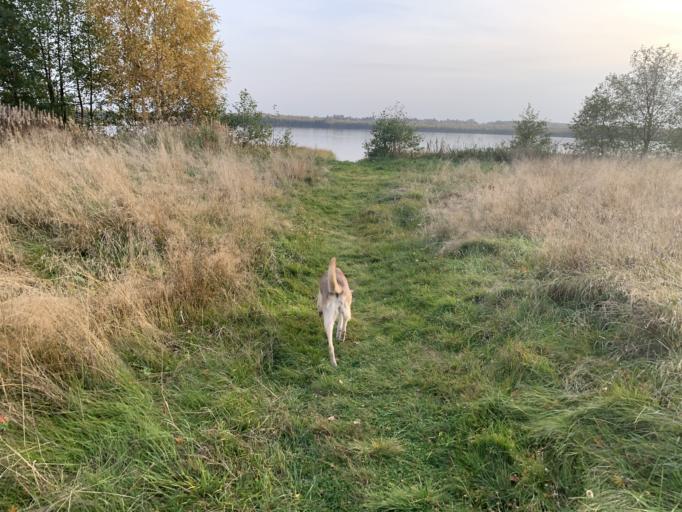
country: RU
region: Jaroslavl
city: Petrovsk
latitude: 56.9800
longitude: 39.3756
